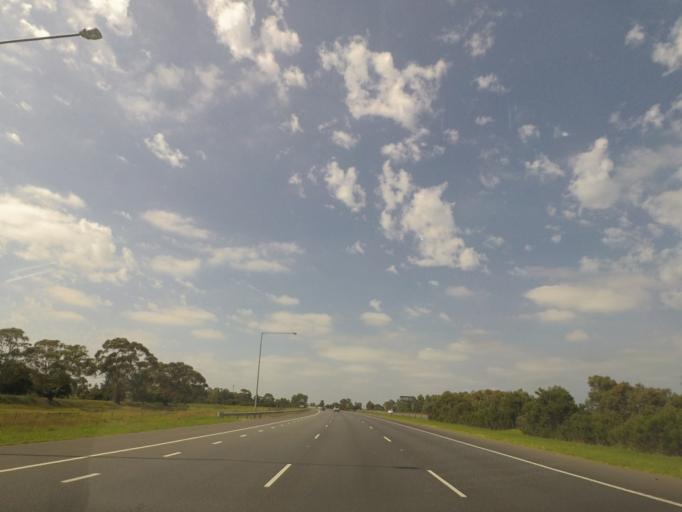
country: AU
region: Victoria
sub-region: Greater Dandenong
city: Keysborough
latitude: -38.0168
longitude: 145.1875
